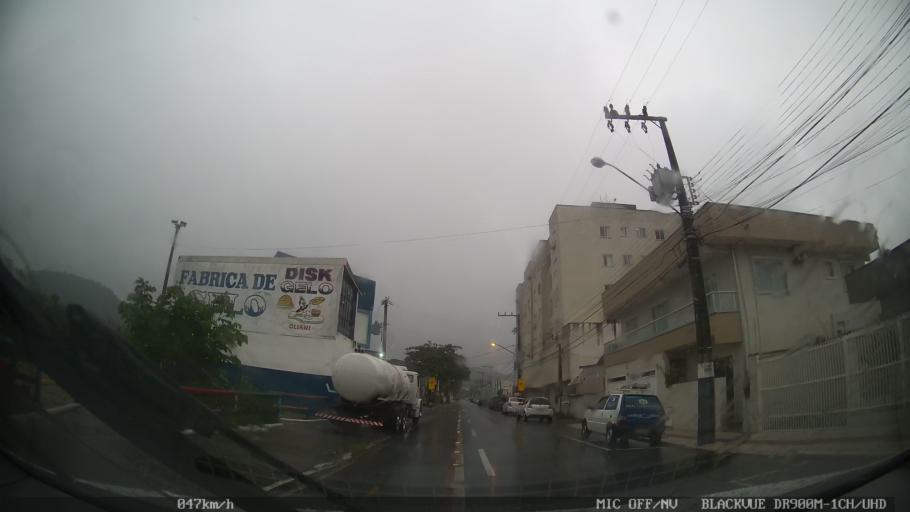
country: BR
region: Santa Catarina
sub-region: Balneario Camboriu
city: Balneario Camboriu
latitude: -27.0115
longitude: -48.6322
